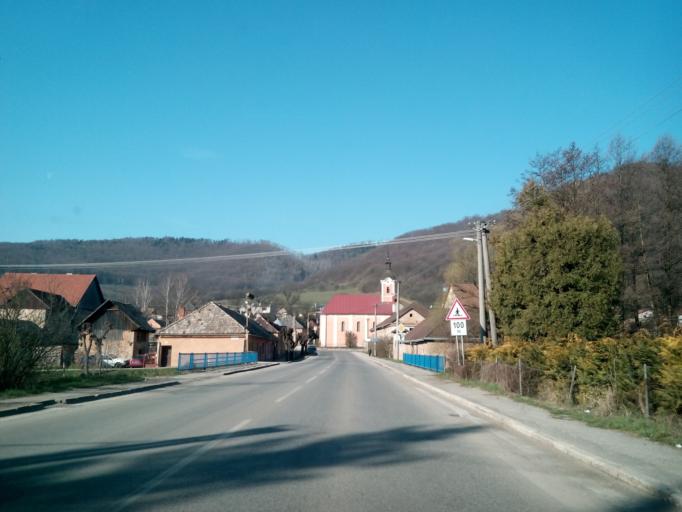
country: SK
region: Kosicky
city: Dobsina
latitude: 48.6603
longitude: 20.3658
